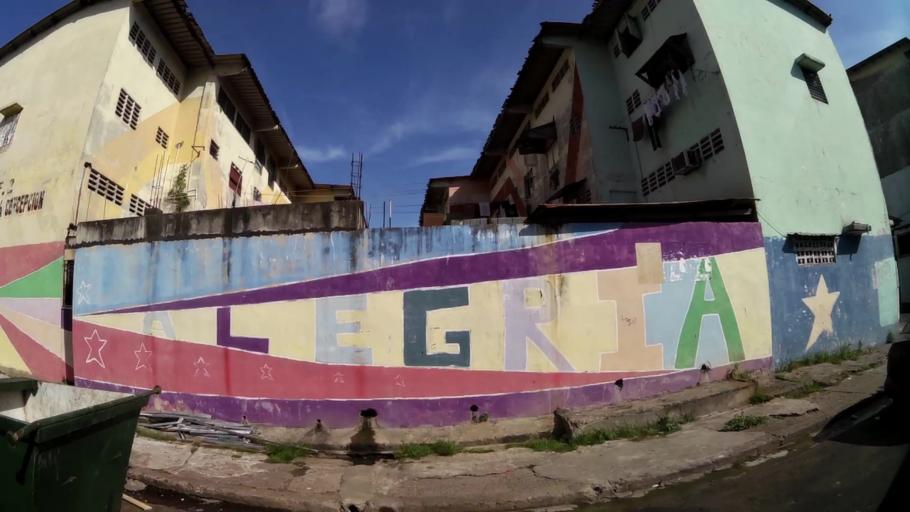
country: PA
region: Panama
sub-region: Distrito de Panama
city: Ancon
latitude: 8.9543
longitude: -79.5417
